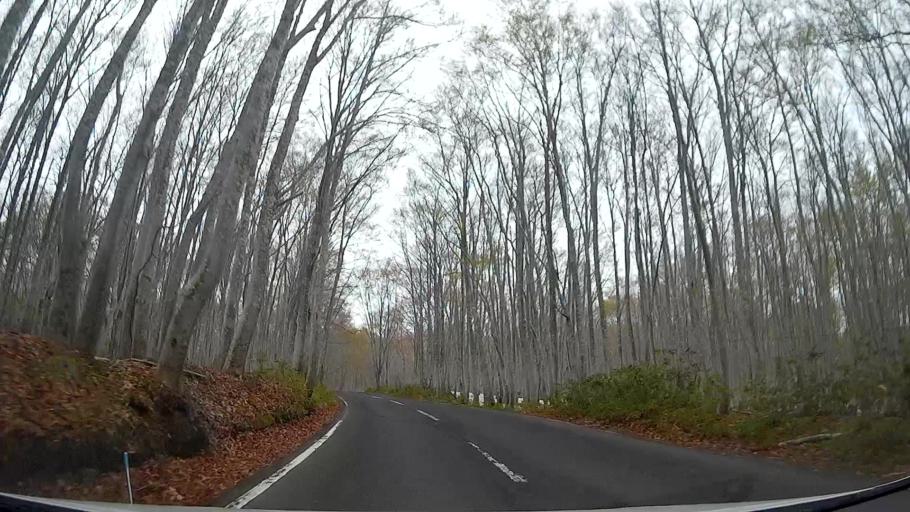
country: JP
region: Aomori
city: Aomori Shi
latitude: 40.6281
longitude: 140.9380
